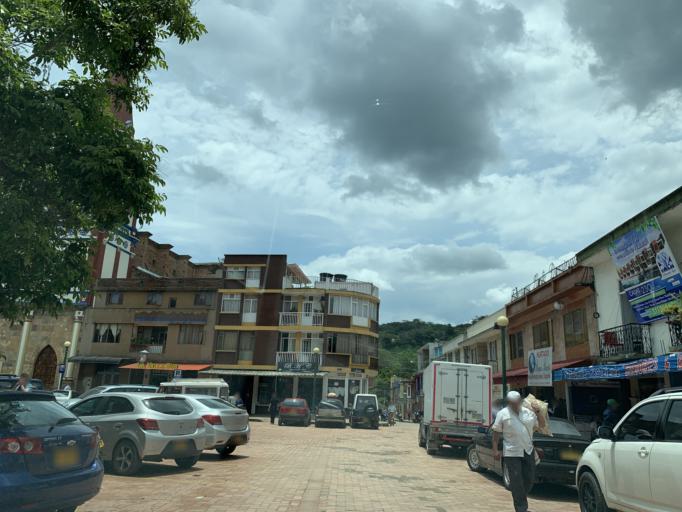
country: CO
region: Boyaca
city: Moniquira
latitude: 5.8775
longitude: -73.5711
